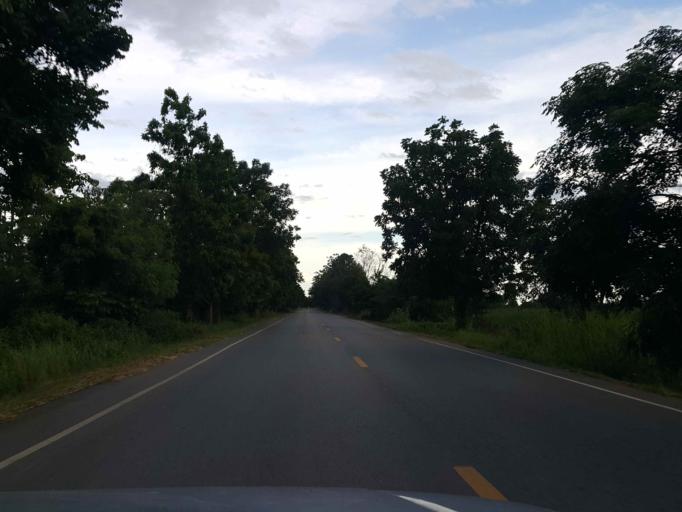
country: TH
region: Sukhothai
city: Sawankhalok
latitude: 17.3769
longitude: 99.7388
